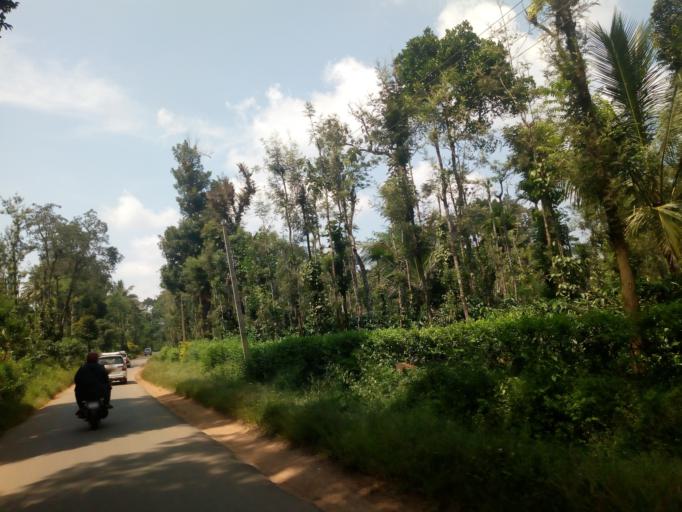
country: IN
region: Karnataka
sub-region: Kodagu
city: Ponnampet
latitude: 12.0307
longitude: 75.9620
